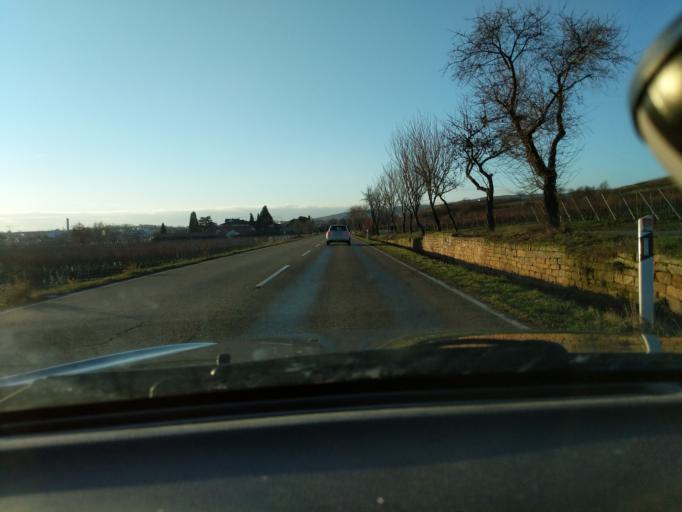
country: DE
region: Rheinland-Pfalz
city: Bad Duerkheim
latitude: 49.4740
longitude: 8.1755
